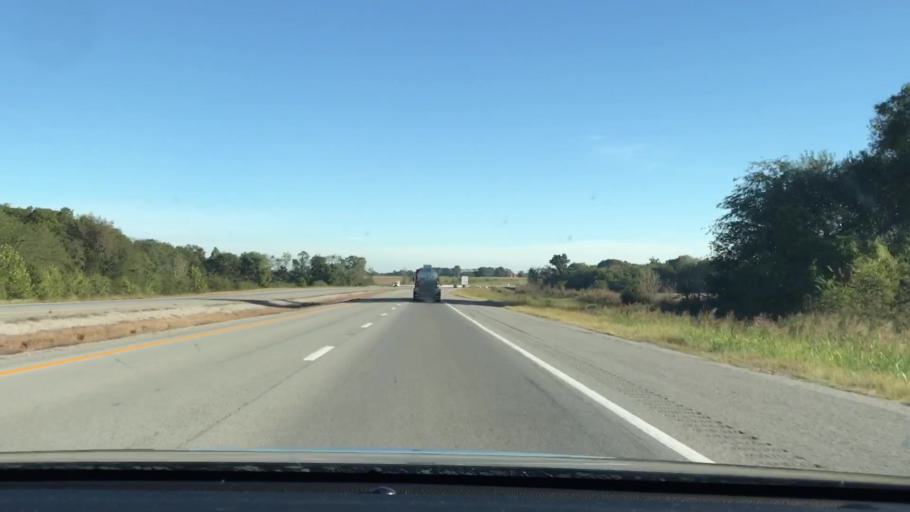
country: US
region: Kentucky
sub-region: Christian County
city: Fort Campbell North
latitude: 36.7498
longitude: -87.5092
